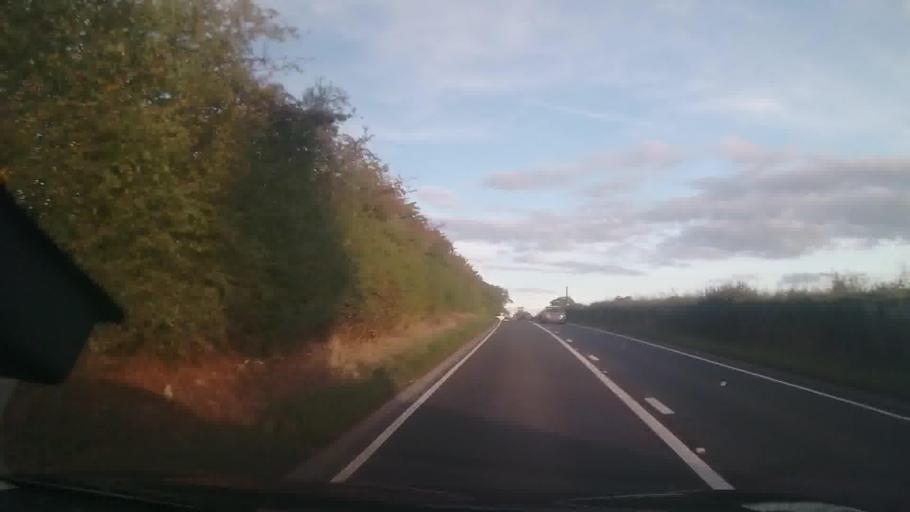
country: GB
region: England
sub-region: Shropshire
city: Westbury
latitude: 52.7068
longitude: -3.0096
